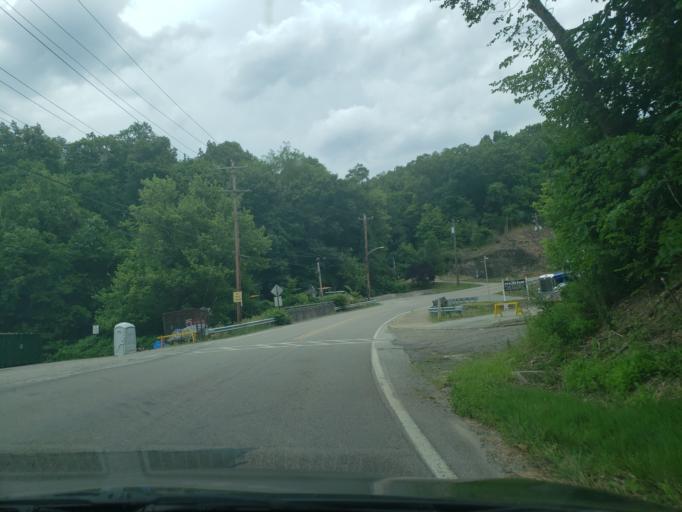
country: US
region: Pennsylvania
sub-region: Allegheny County
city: Avalon
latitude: 40.5035
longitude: -80.0657
